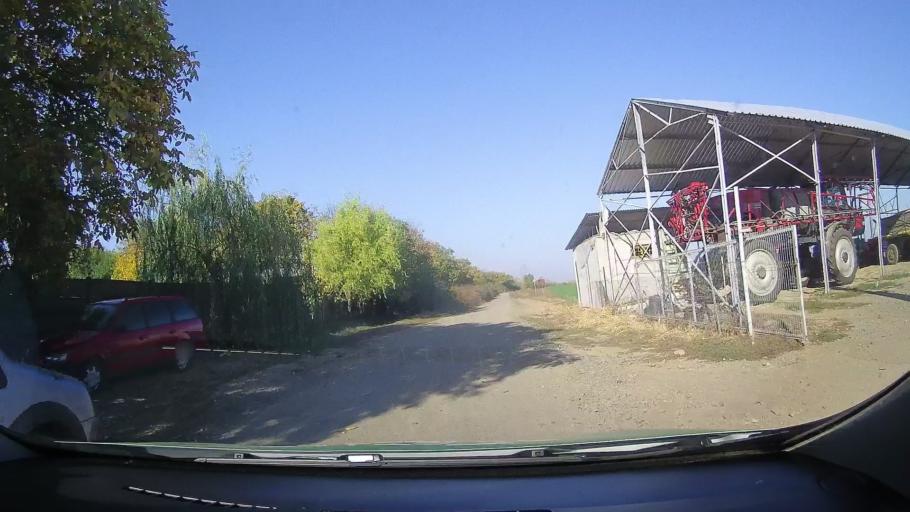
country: RO
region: Satu Mare
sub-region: Comuna Sauca
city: Sauca
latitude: 47.4725
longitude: 22.4839
